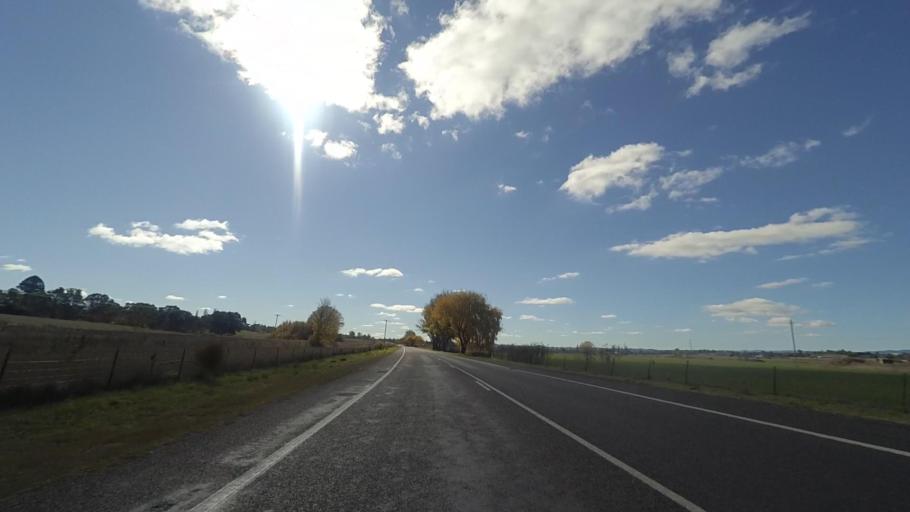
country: AU
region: New South Wales
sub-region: Bathurst Regional
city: Bathurst
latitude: -33.4505
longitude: 149.5789
